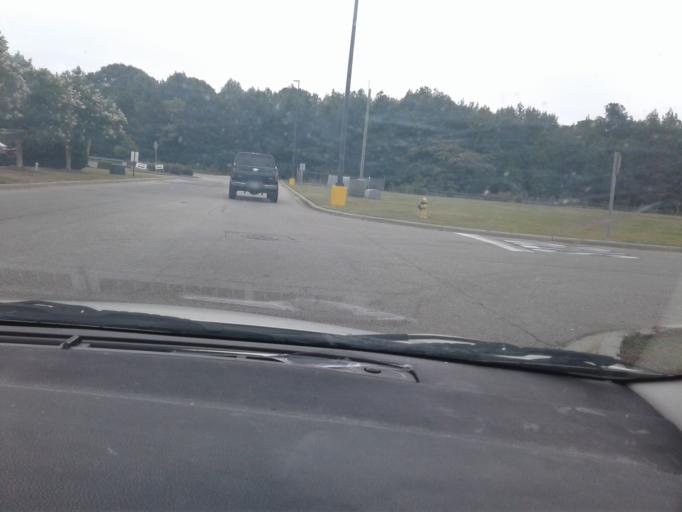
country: US
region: North Carolina
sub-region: Harnett County
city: Erwin
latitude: 35.3226
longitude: -78.6461
